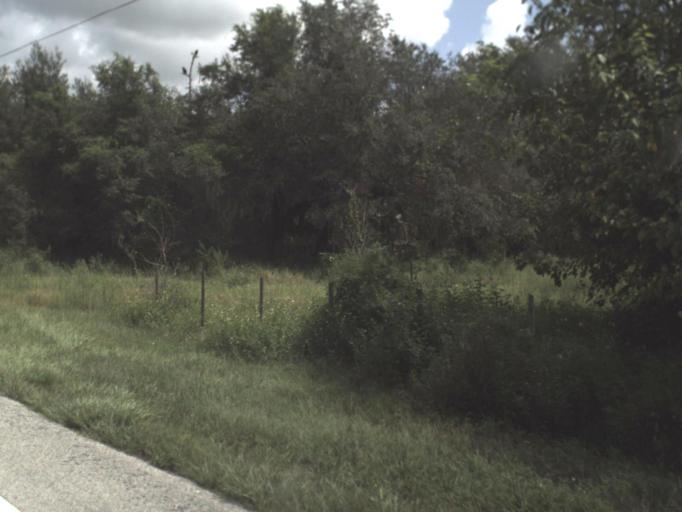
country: US
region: Florida
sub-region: DeSoto County
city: Arcadia
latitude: 27.3466
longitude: -81.8034
